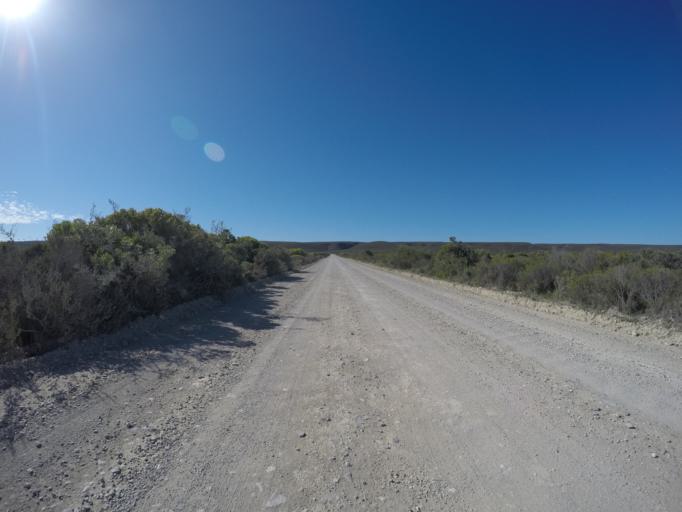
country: ZA
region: Western Cape
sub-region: Overberg District Municipality
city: Bredasdorp
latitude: -34.4391
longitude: 20.4208
